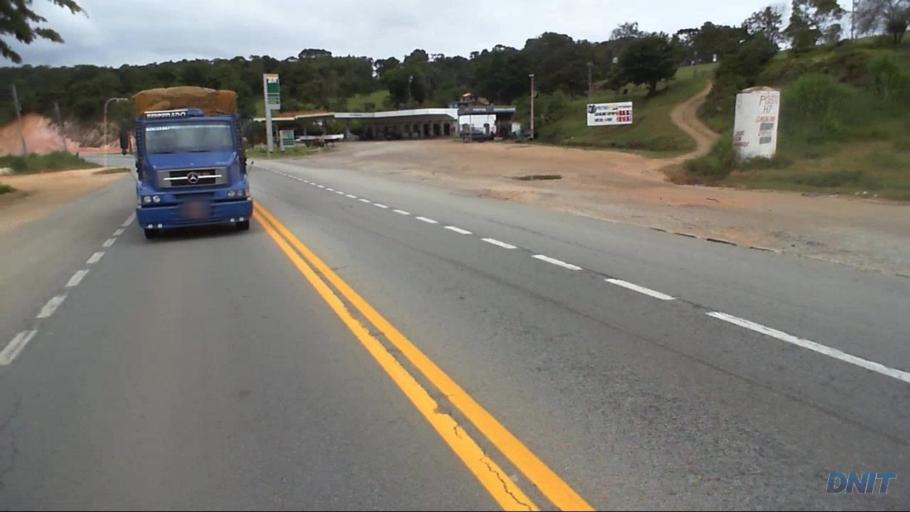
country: BR
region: Minas Gerais
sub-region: Caete
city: Caete
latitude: -19.7400
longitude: -43.5563
